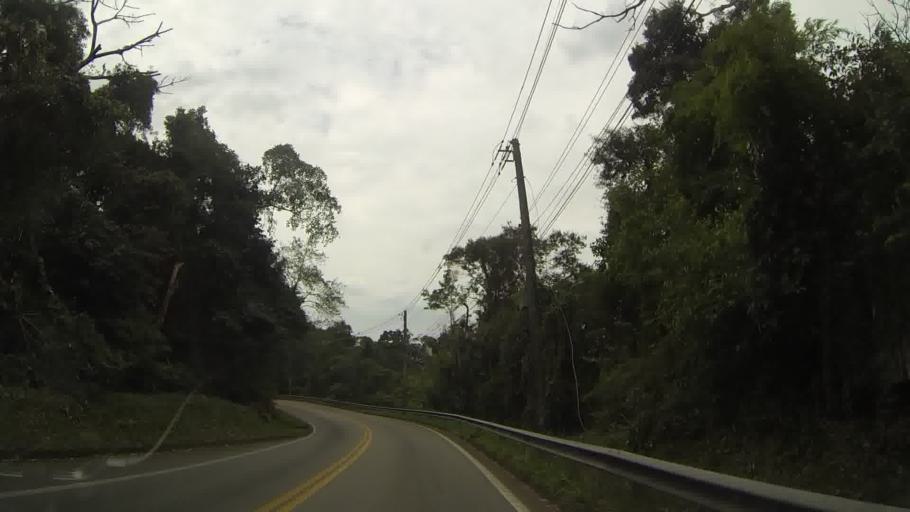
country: BR
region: Sao Paulo
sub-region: Sao Sebastiao
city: Sao Sebastiao
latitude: -23.8225
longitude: -45.4776
